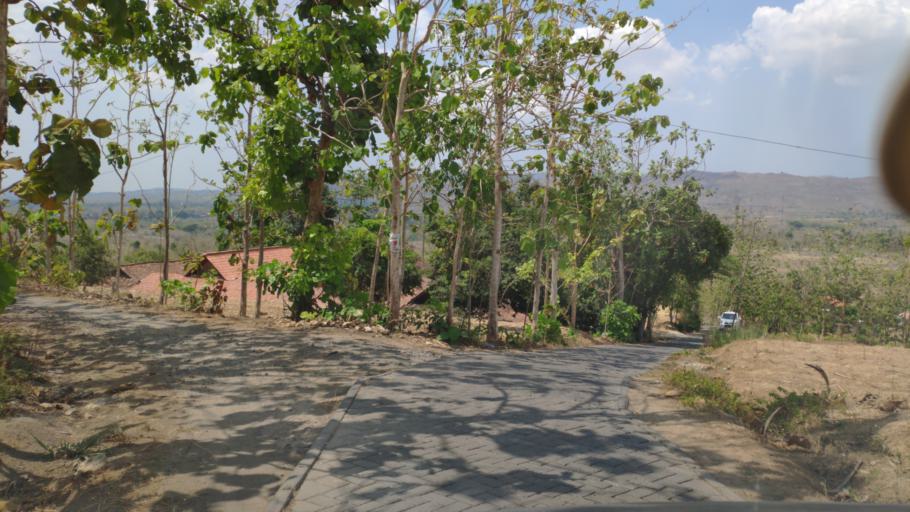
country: ID
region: Central Java
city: Banyubang
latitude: -6.9528
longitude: 111.5210
